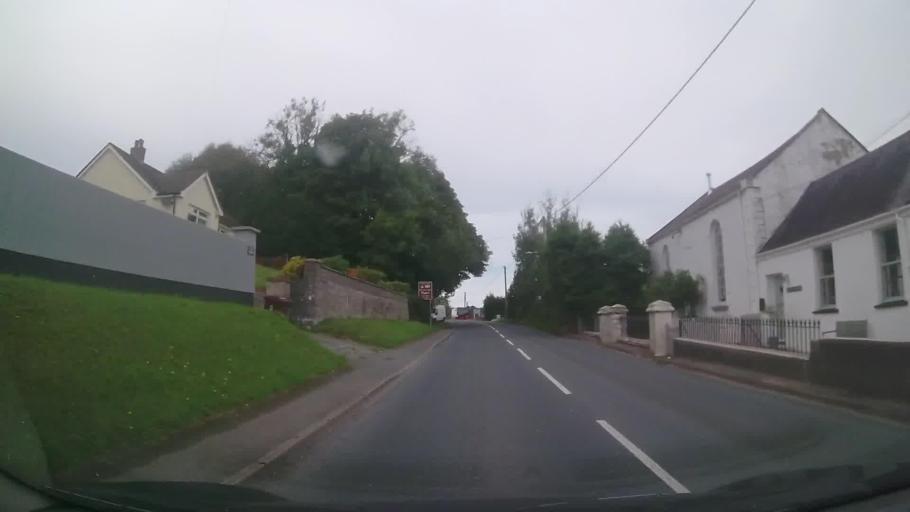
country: GB
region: Wales
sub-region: Pembrokeshire
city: Kilgetty
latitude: 51.7352
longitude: -4.7269
